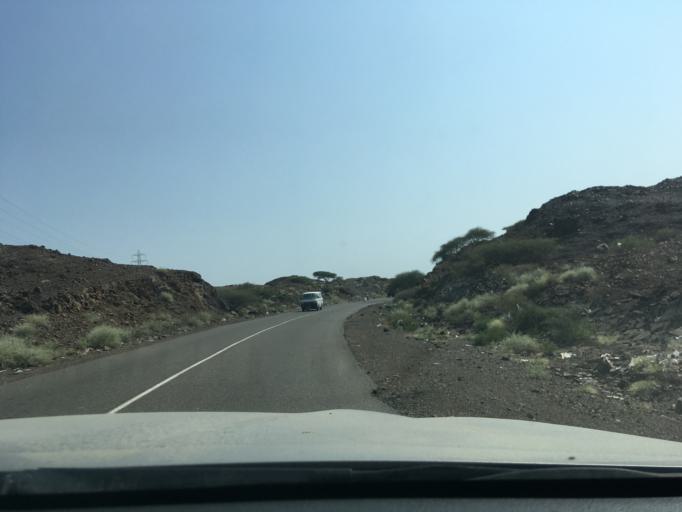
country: YE
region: Lahij
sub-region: Al Milah
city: Al Milah
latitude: 13.3835
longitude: 44.8095
